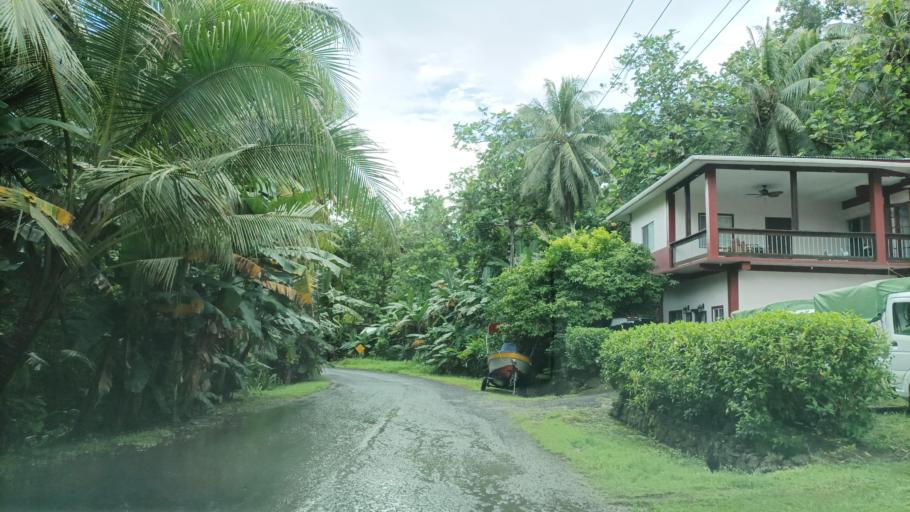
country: FM
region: Pohnpei
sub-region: Madolenihm Municipality
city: Madolenihm Municipality Government
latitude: 6.9126
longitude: 158.3224
